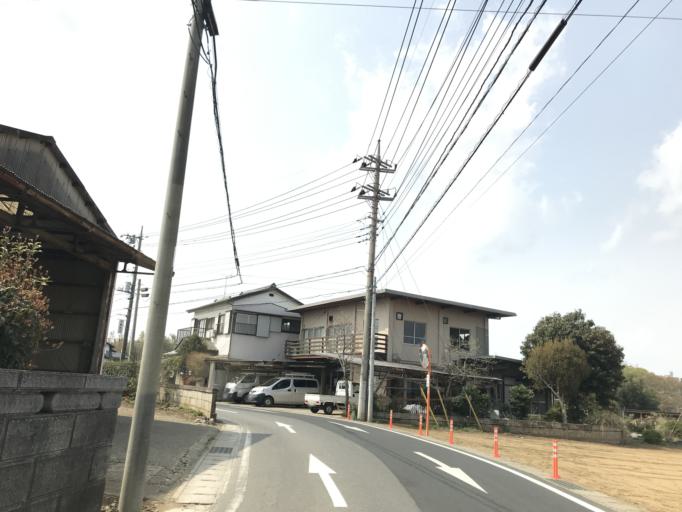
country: JP
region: Ibaraki
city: Moriya
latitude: 35.9840
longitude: 140.0445
